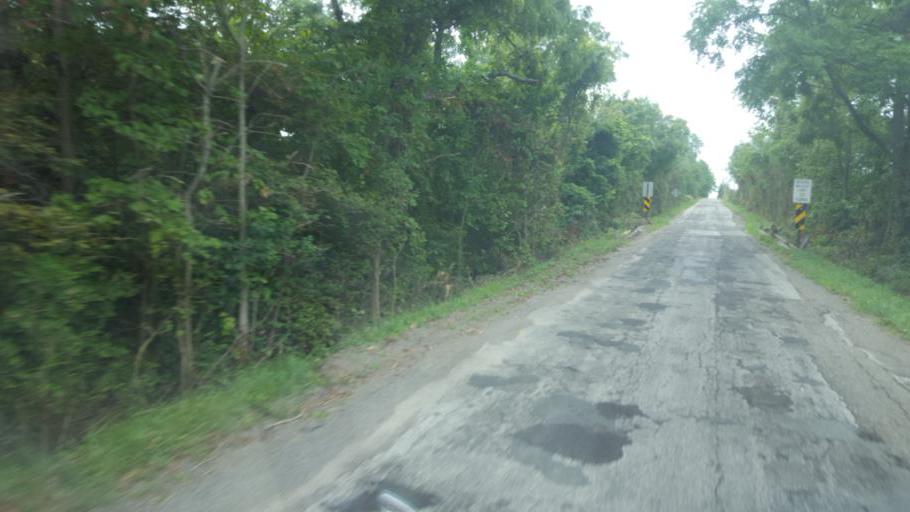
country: US
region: Ohio
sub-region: Morrow County
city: Mount Gilead
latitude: 40.6053
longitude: -82.8423
